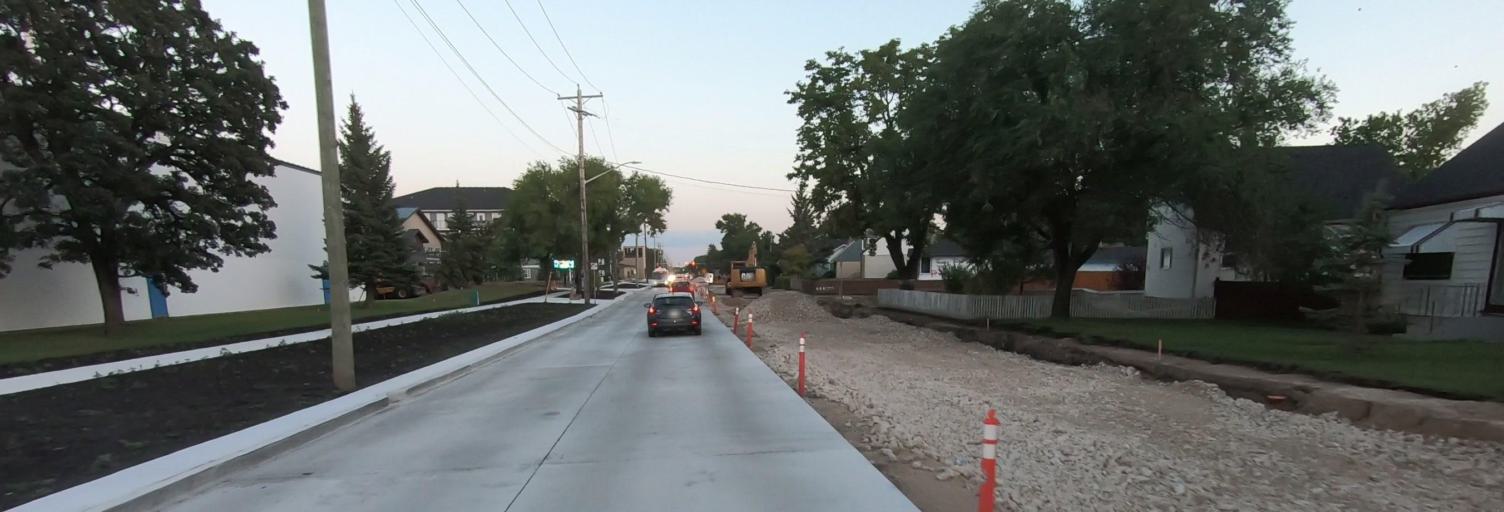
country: CA
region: Manitoba
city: Winnipeg
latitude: 49.8793
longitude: -97.0974
